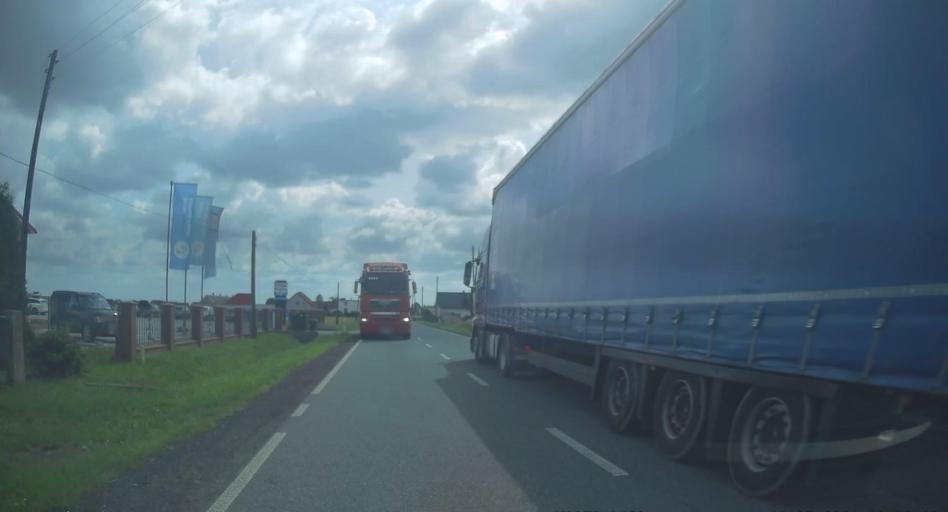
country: PL
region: Opole Voivodeship
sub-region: Powiat prudnicki
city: Glogowek
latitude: 50.3451
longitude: 17.8955
